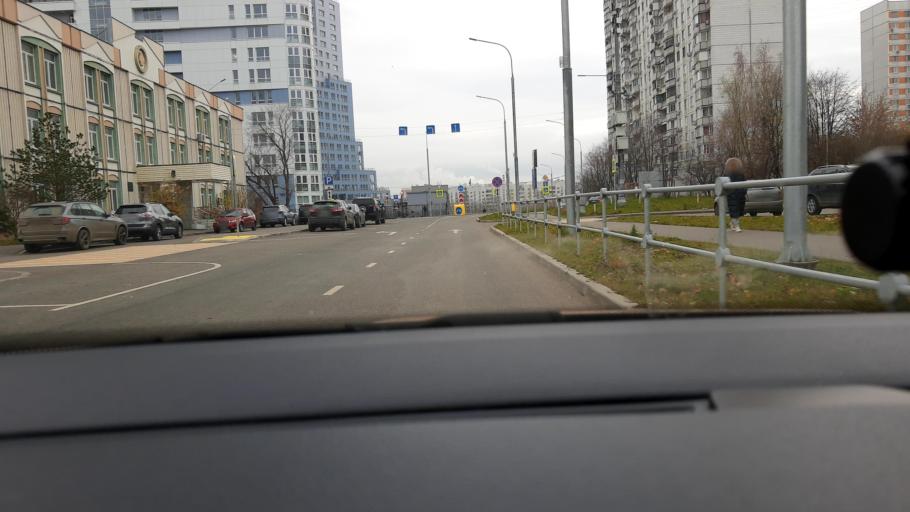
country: RU
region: Moskovskaya
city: Khoroshevo-Mnevniki
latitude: 55.7710
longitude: 37.4942
